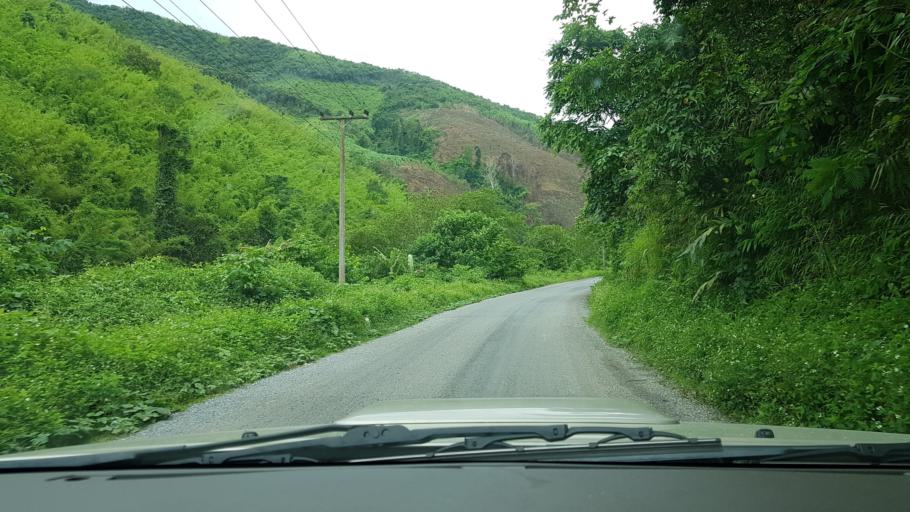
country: LA
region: Oudomxai
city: Muang La
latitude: 21.0430
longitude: 102.2415
